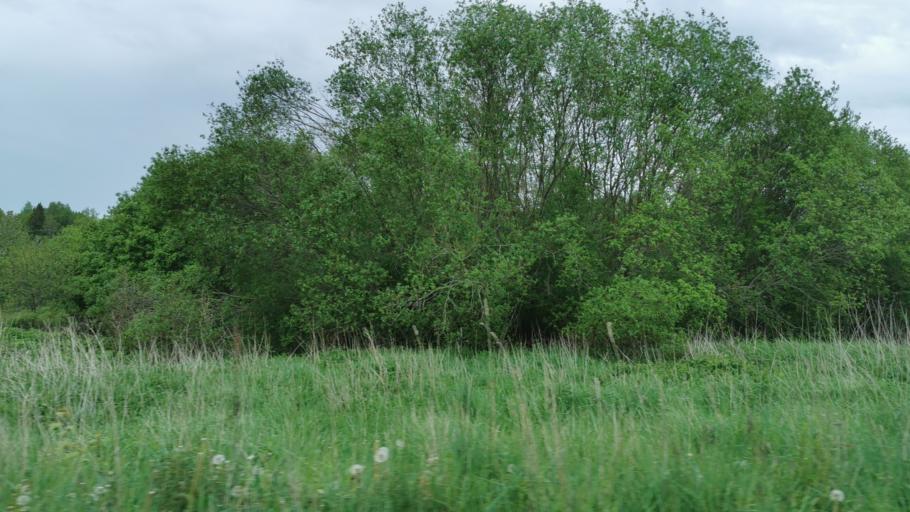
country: EE
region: Laeaene-Virumaa
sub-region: Rakvere linn
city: Rakvere
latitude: 59.2731
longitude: 26.3508
